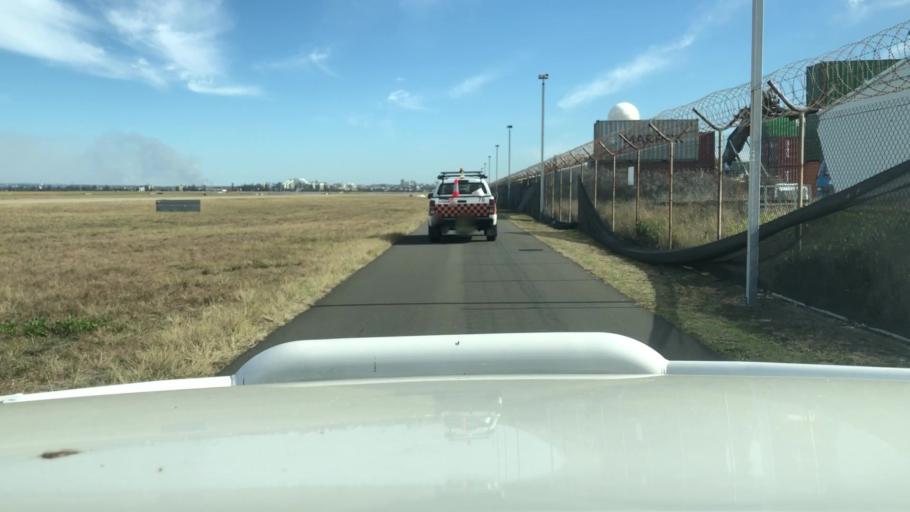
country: AU
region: New South Wales
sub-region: Botany Bay
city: Botany
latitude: -33.9498
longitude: 151.1849
